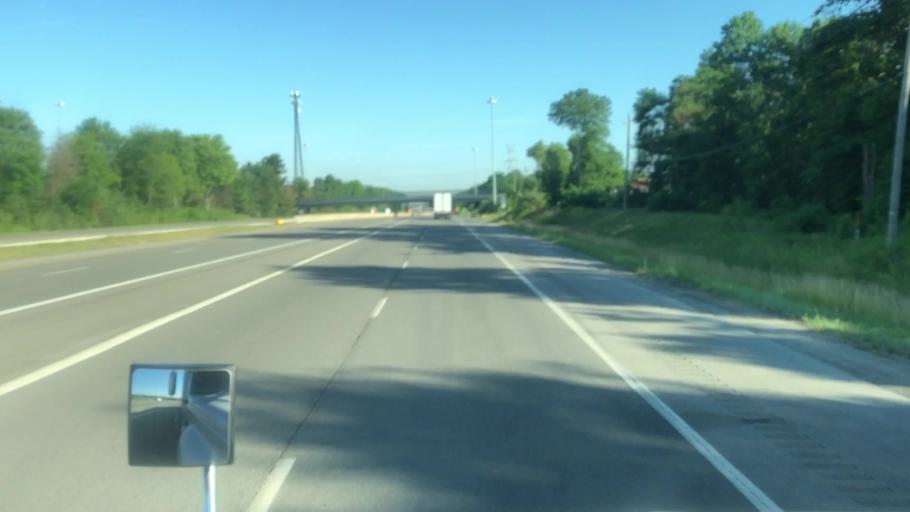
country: US
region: Ohio
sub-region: Trumbull County
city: Lordstown
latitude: 41.1156
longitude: -80.8420
